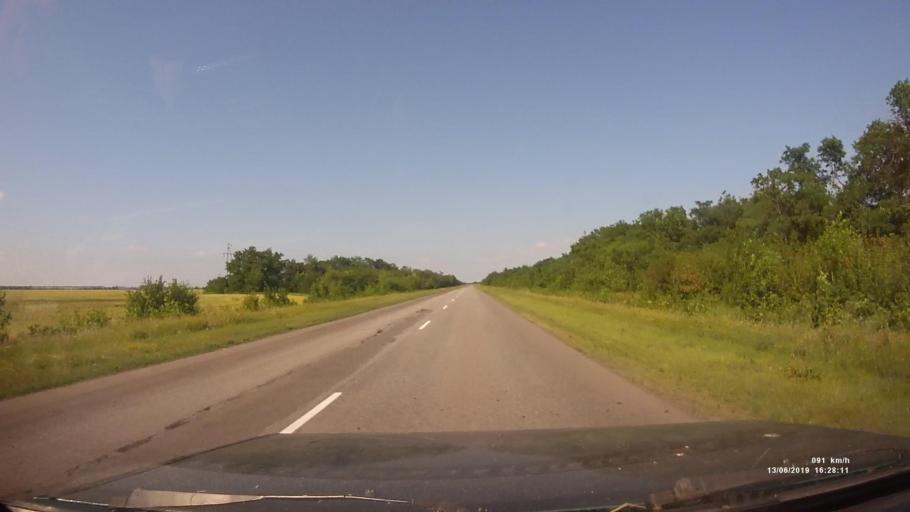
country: RU
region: Rostov
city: Kazanskaya
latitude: 49.8195
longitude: 41.1956
